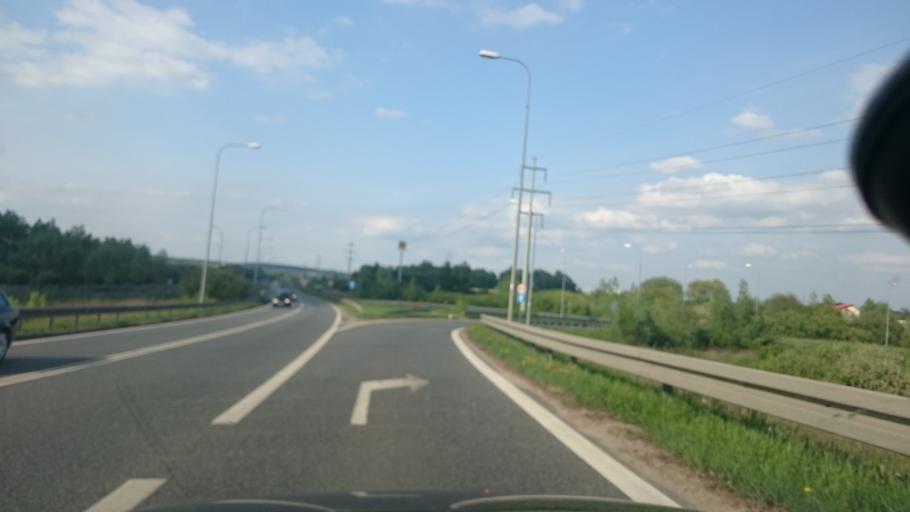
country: PL
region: Kujawsko-Pomorskie
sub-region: Grudziadz
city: Grudziadz
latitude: 53.4843
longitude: 18.7921
